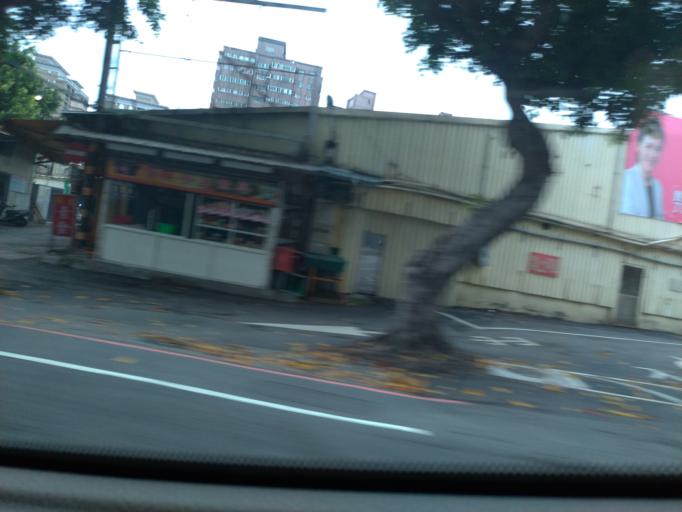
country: TW
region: Taiwan
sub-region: Taoyuan
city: Taoyuan
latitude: 24.9336
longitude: 121.3753
